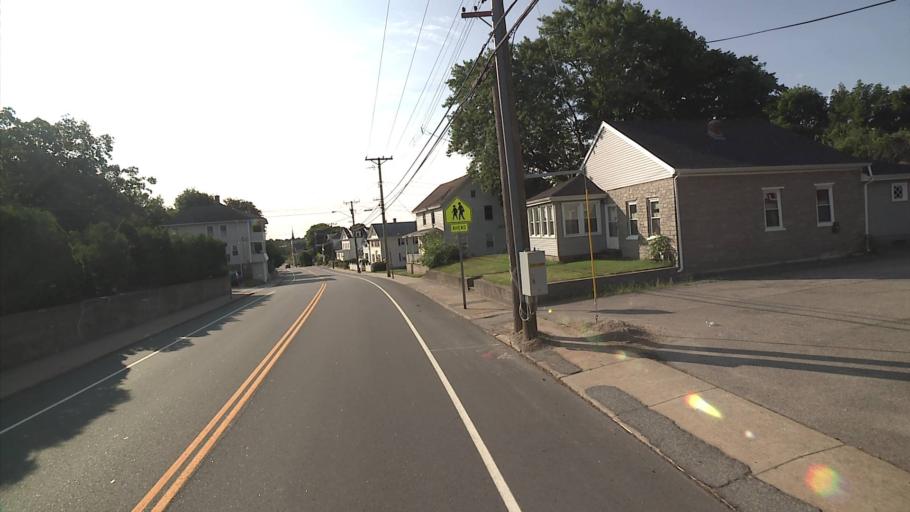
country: US
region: Connecticut
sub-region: New London County
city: Pawcatuck
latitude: 41.3820
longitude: -71.8414
